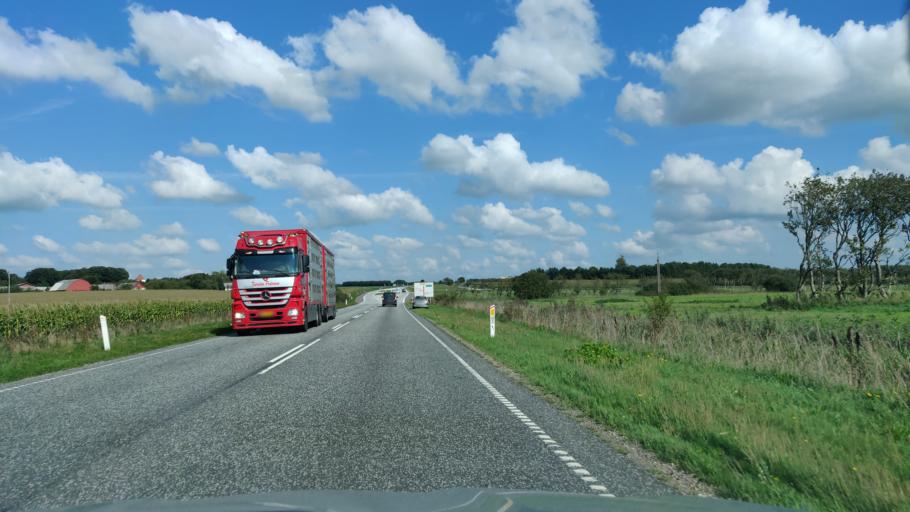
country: DK
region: North Denmark
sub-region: Vesthimmerland Kommune
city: Aars
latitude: 56.8061
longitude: 9.6479
